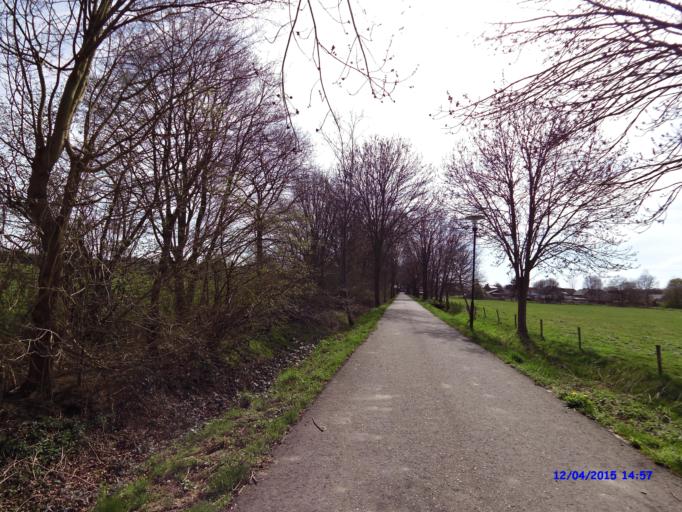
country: DE
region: North Rhine-Westphalia
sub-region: Regierungsbezirk Koln
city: Gangelt
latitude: 50.9832
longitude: 6.0327
